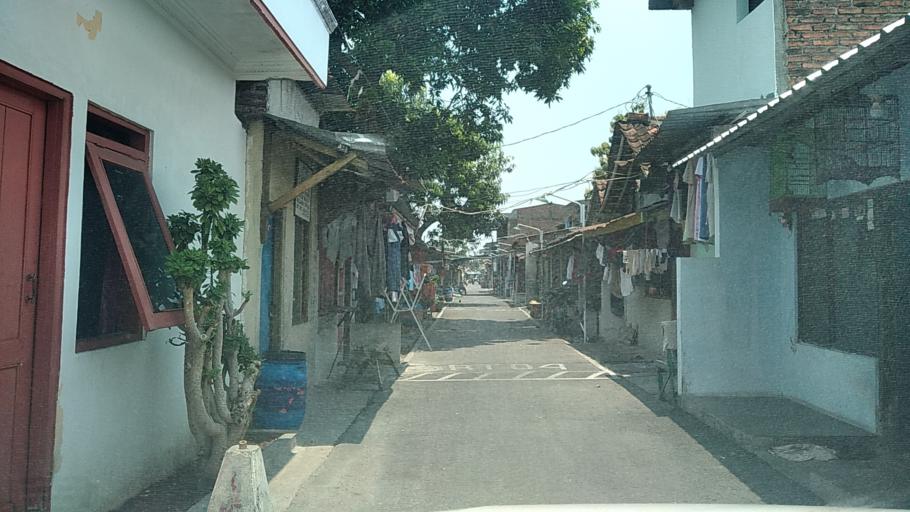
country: ID
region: Central Java
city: Semarang
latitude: -7.0010
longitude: 110.4418
